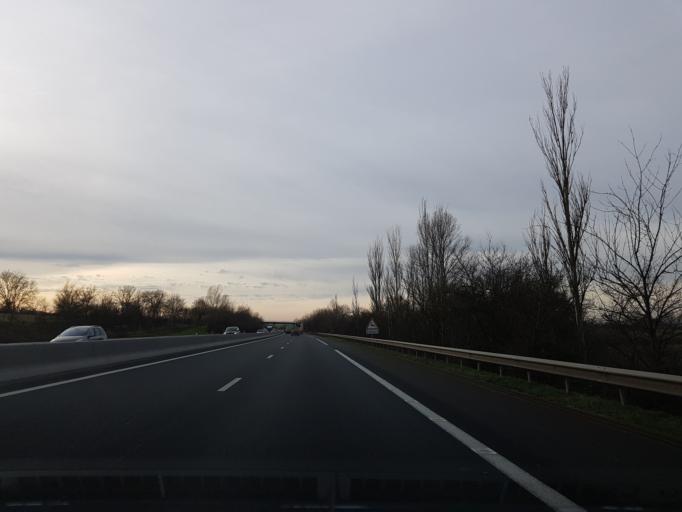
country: FR
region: Auvergne
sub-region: Departement de l'Allier
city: Montmarault
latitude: 46.3293
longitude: 2.9500
